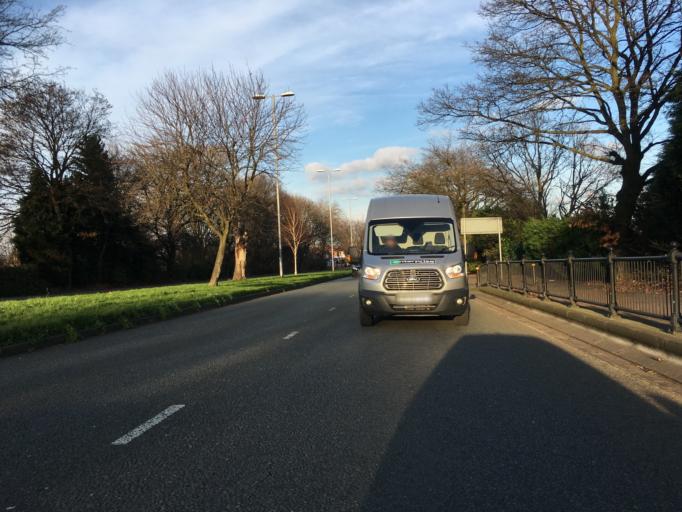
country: GB
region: England
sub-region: Manchester
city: Didsbury
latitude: 53.4126
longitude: -2.2181
